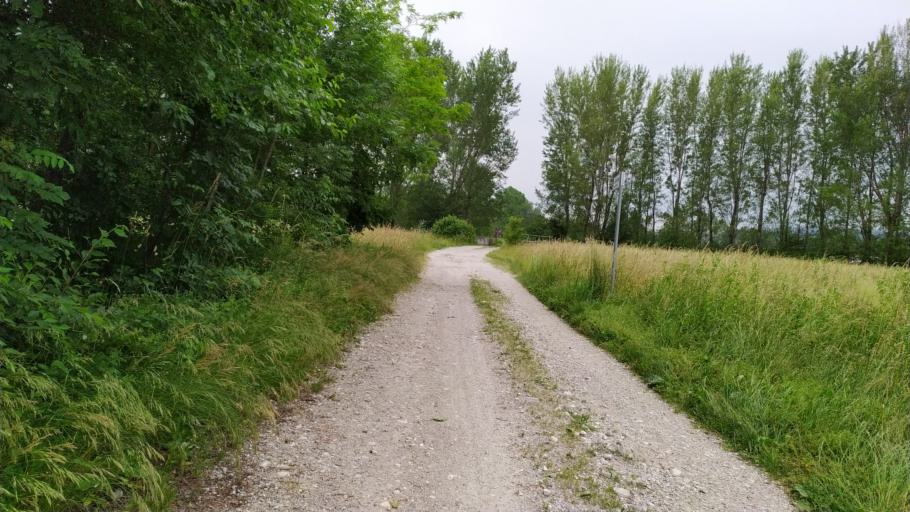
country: IT
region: Friuli Venezia Giulia
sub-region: Provincia di Udine
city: Majano
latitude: 46.2168
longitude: 13.0627
